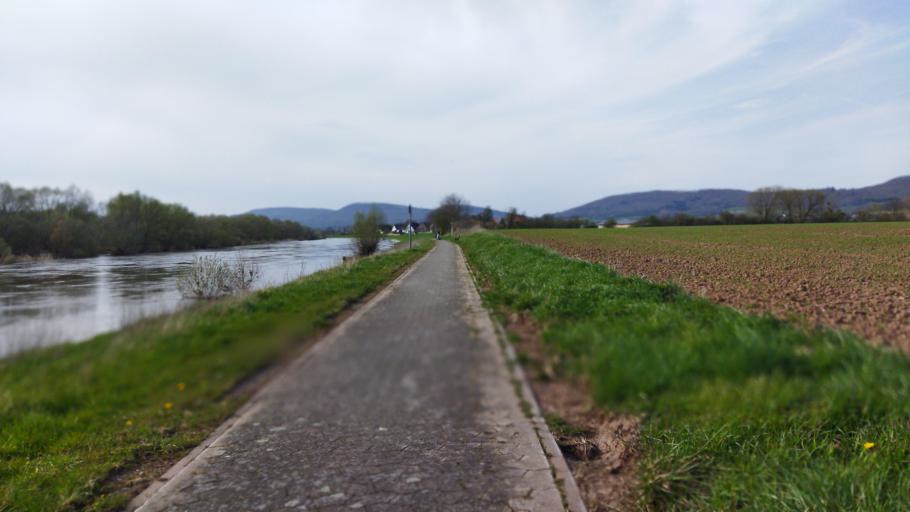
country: DE
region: Lower Saxony
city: Buchholz
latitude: 52.1812
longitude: 9.1578
